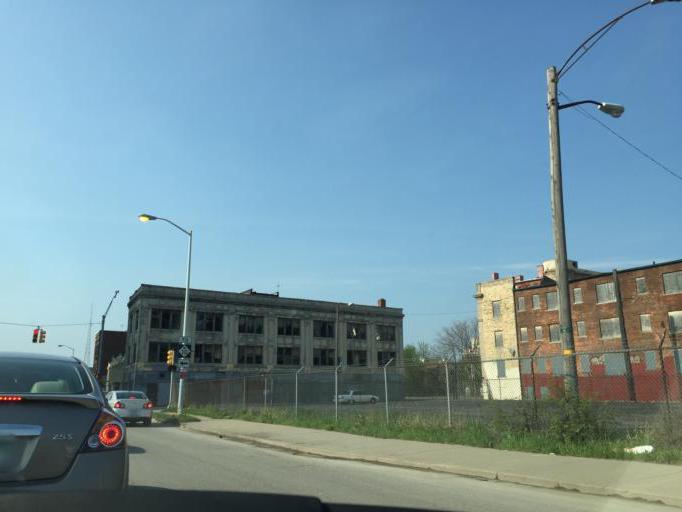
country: US
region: Michigan
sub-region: Wayne County
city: Detroit
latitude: 42.3413
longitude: -83.0583
